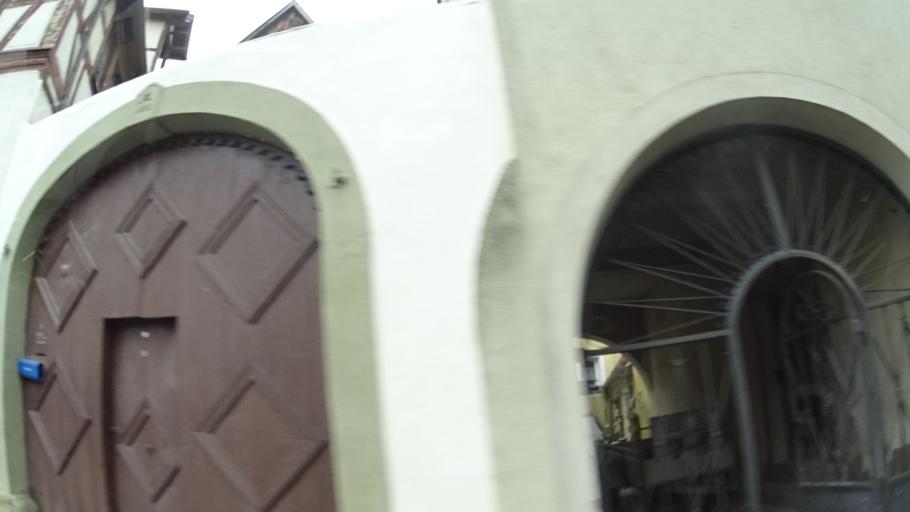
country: DE
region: Bavaria
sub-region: Regierungsbezirk Unterfranken
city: Frickenhausen
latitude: 49.6707
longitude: 10.0954
